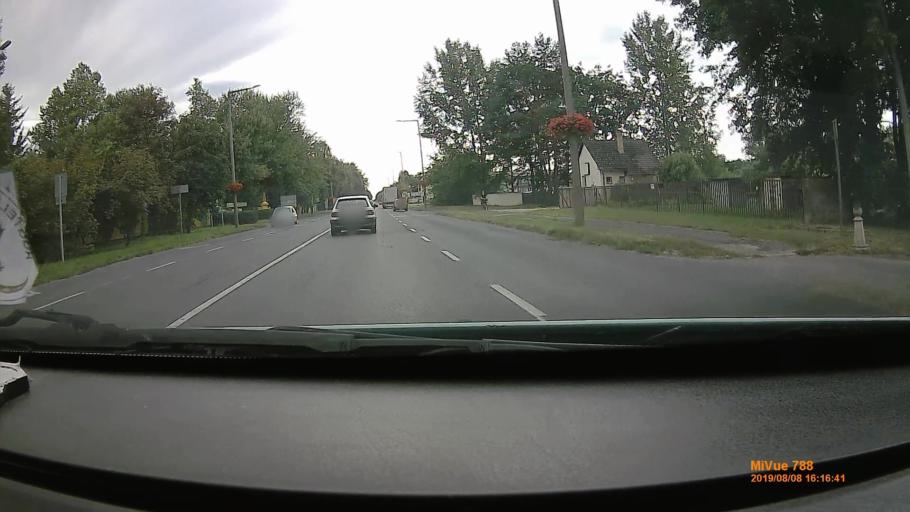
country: HU
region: Szabolcs-Szatmar-Bereg
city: Mateszalka
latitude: 47.9619
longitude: 22.3022
